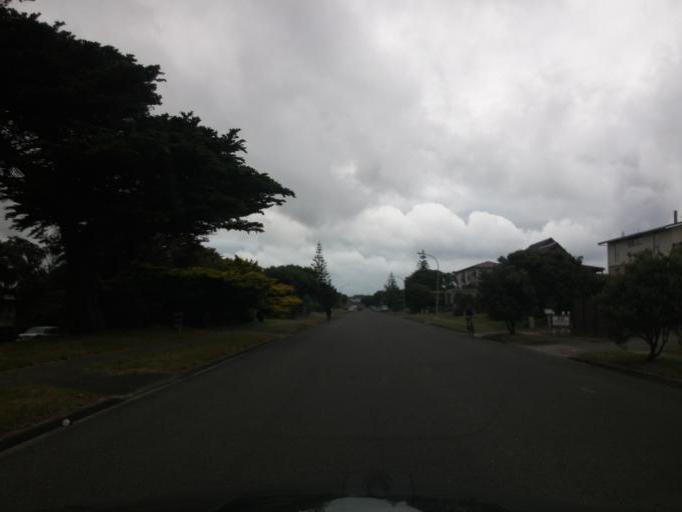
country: NZ
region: Wellington
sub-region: Kapiti Coast District
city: Paraparaumu
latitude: -40.8655
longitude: 175.0177
